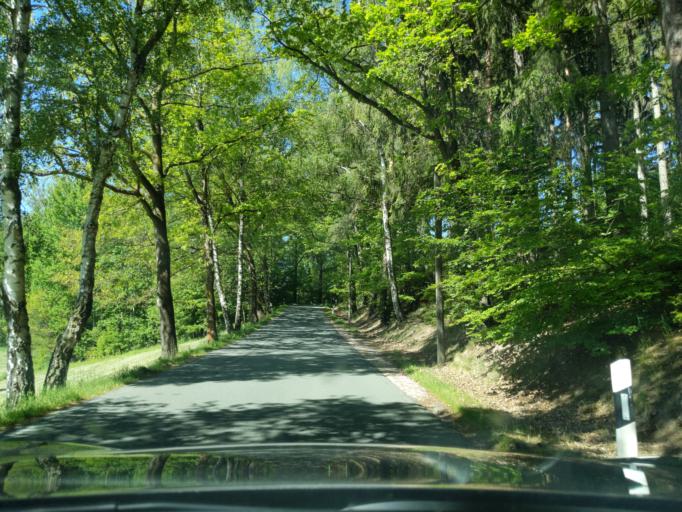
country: DE
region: Saxony
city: Hirschfeld
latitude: 50.5754
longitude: 12.4758
